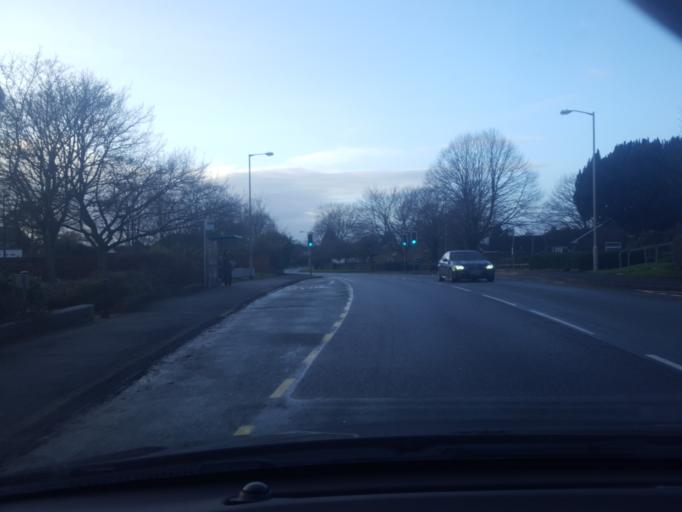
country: GB
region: England
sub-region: Staffordshire
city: Codsall
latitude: 52.6310
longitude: -2.2000
